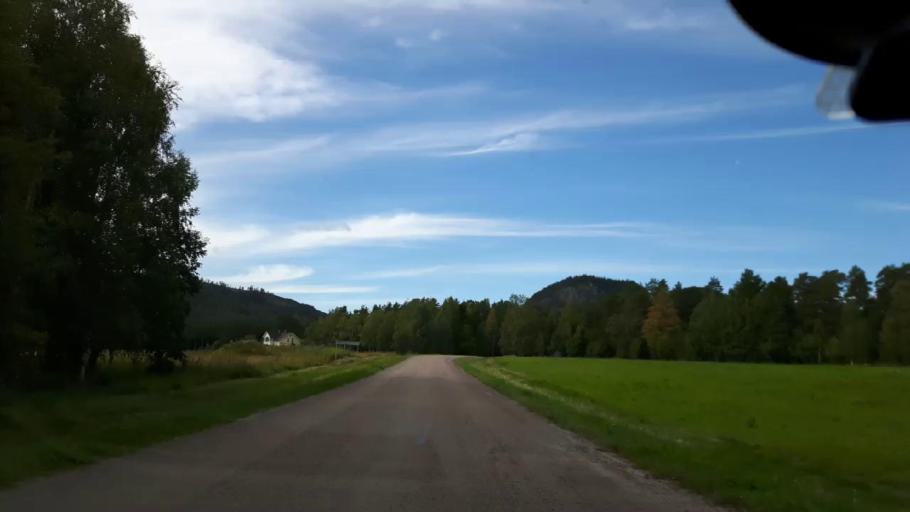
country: SE
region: Jaemtland
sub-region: Ragunda Kommun
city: Hammarstrand
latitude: 63.1161
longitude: 16.3437
